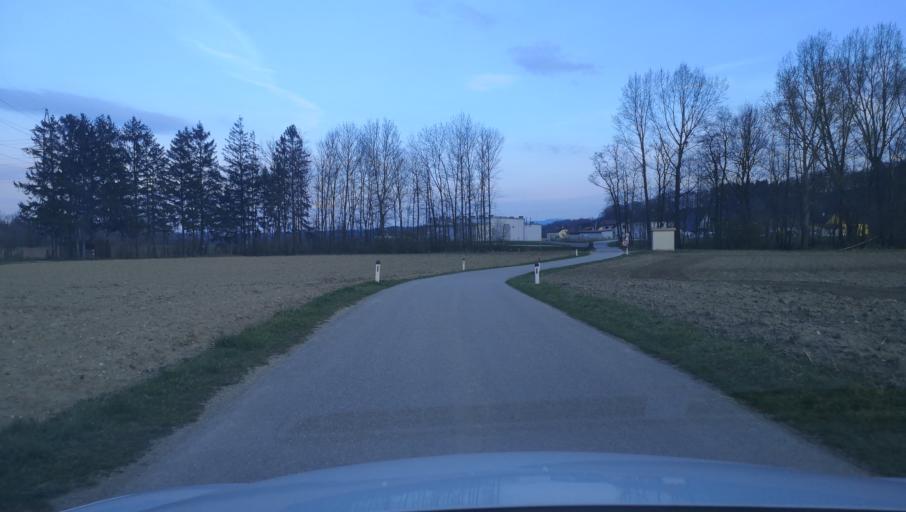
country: AT
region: Lower Austria
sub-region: Politischer Bezirk Amstetten
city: Euratsfeld
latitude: 48.1038
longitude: 14.9039
